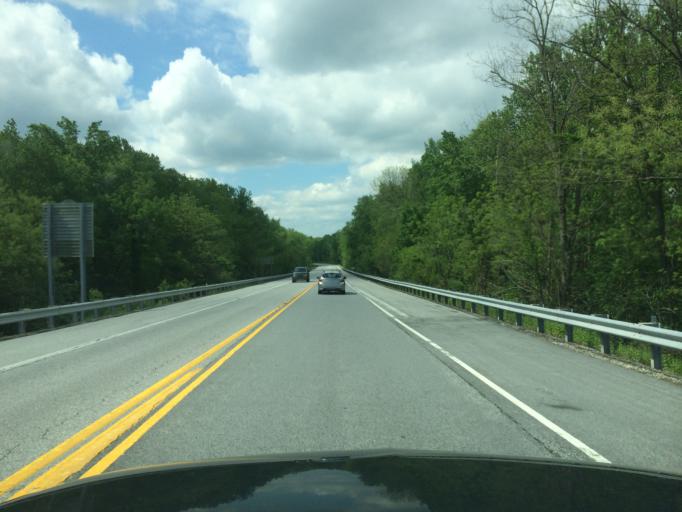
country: US
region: Maryland
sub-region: Carroll County
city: Westminster
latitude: 39.5197
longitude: -76.9913
